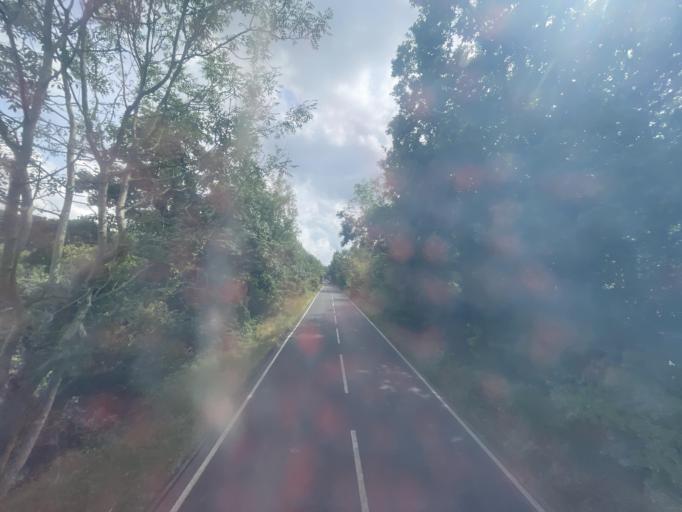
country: GB
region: England
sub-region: Greater London
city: Bromley
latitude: 51.3666
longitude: 0.0253
